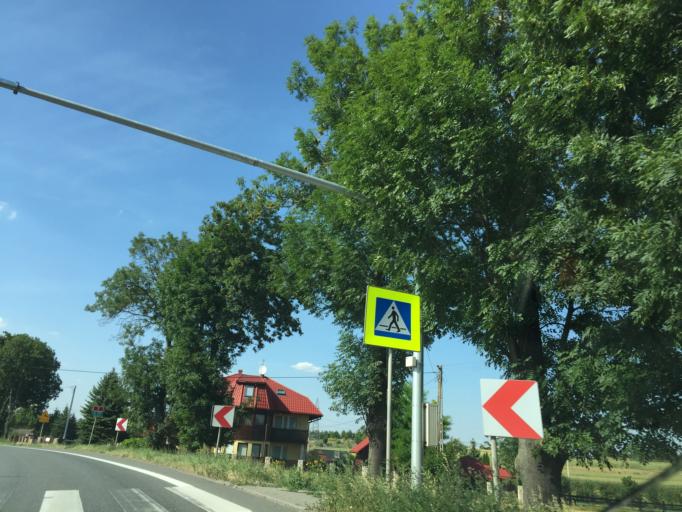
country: PL
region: Lesser Poland Voivodeship
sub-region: Powiat krakowski
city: Slomniki
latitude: 50.2524
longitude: 20.0882
